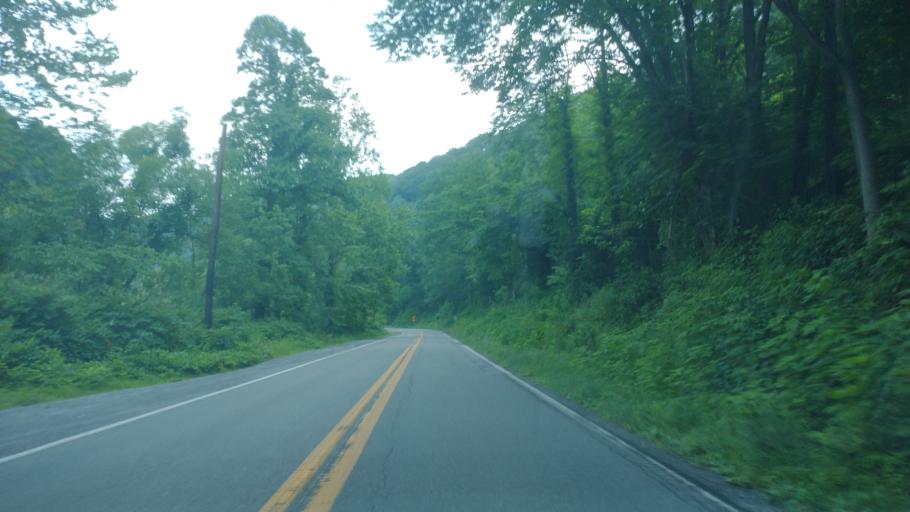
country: US
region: West Virginia
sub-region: McDowell County
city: Welch
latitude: 37.4081
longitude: -81.4682
